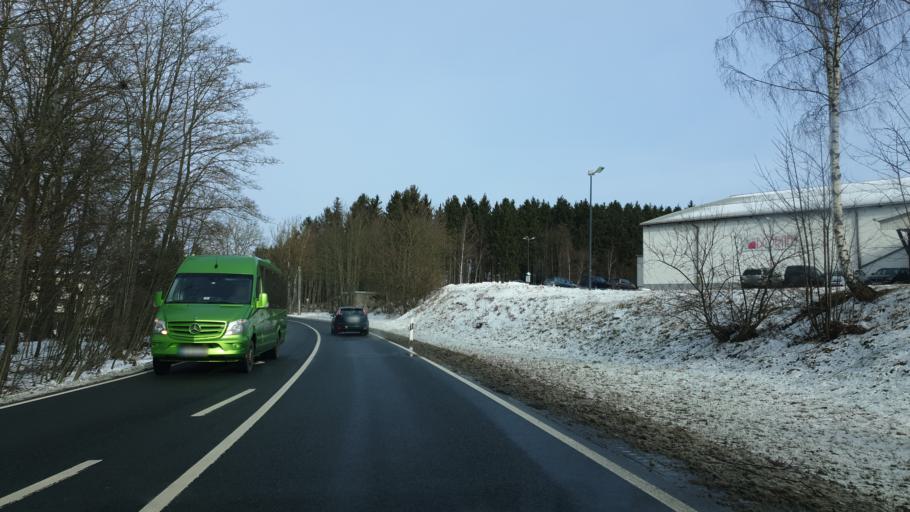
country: DE
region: Saxony
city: Triebel
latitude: 50.3846
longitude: 12.1502
